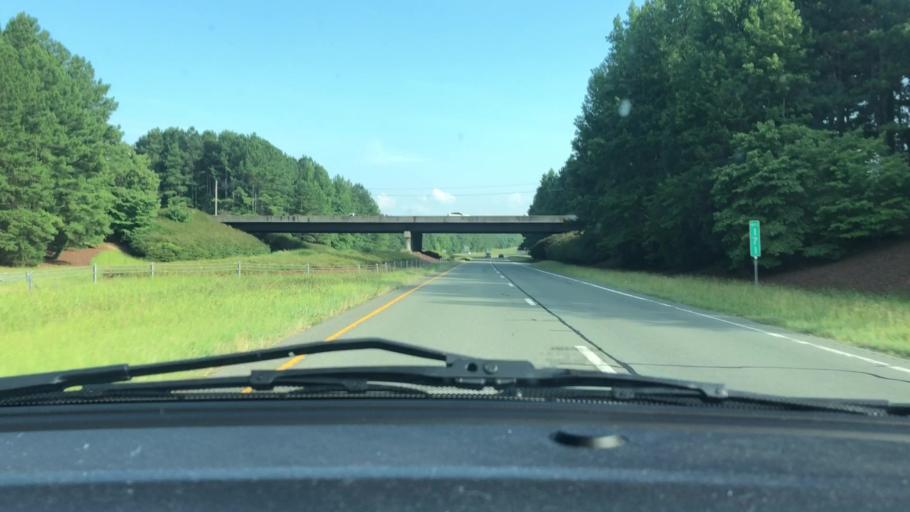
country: US
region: North Carolina
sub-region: Chatham County
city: Siler City
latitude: 35.7355
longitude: -79.4325
